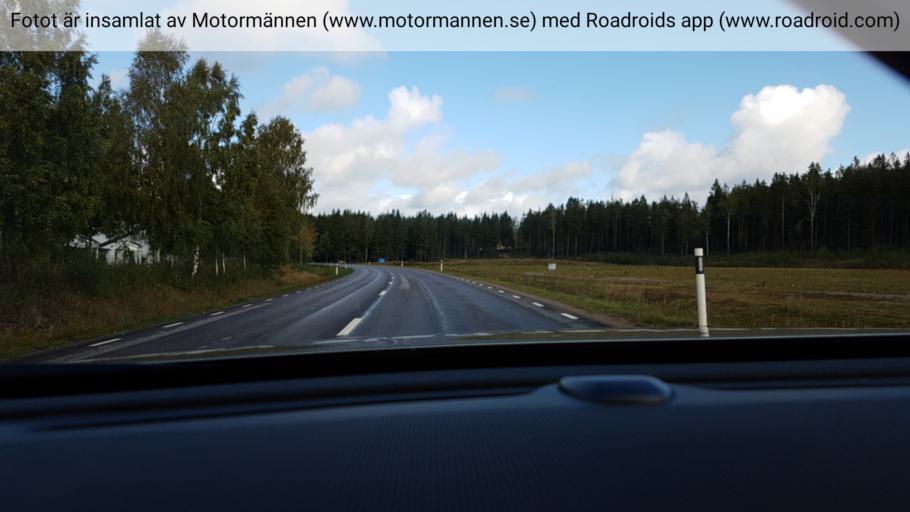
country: SE
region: Vaestra Goetaland
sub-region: Svenljunga Kommun
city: Svenljunga
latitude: 57.4861
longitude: 13.1178
